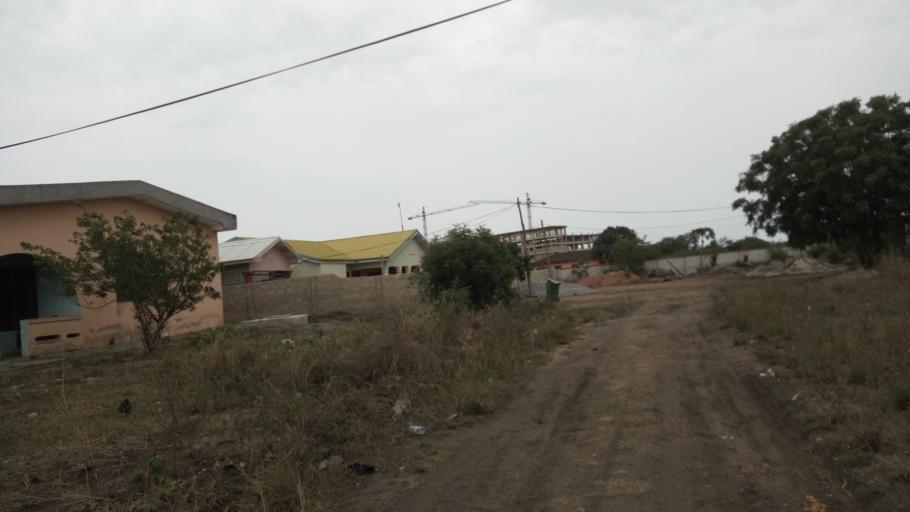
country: GH
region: Central
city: Winneba
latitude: 5.3740
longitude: -0.6336
